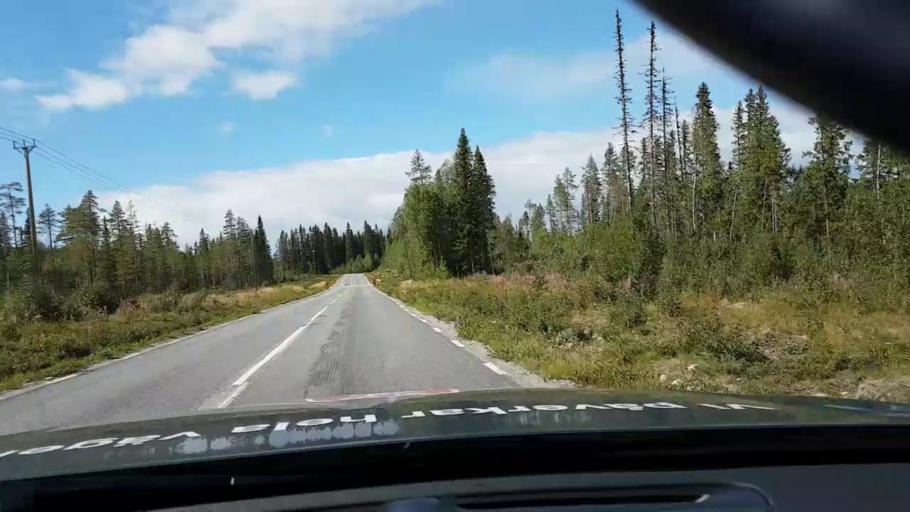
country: SE
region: Vaesterbotten
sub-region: Asele Kommun
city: Asele
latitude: 63.8230
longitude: 17.4815
